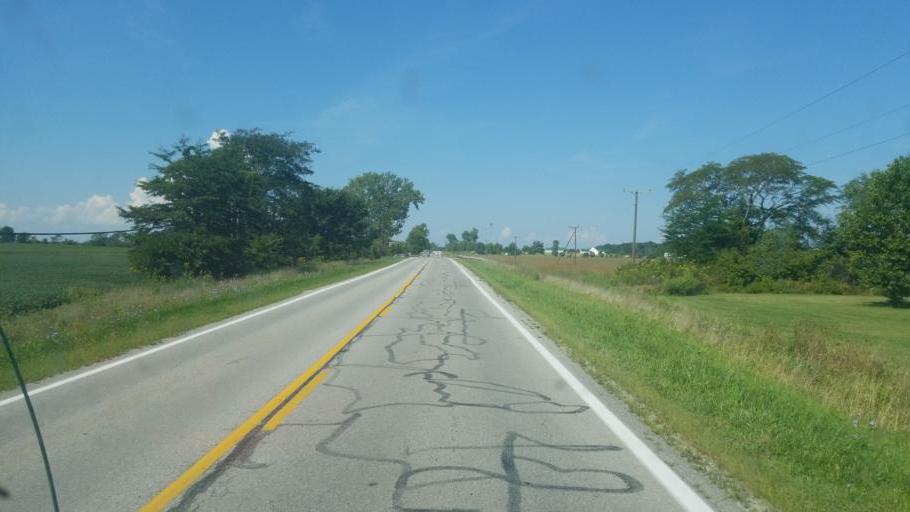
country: US
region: Ohio
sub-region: Marion County
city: Marion
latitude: 40.6126
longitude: -83.1889
